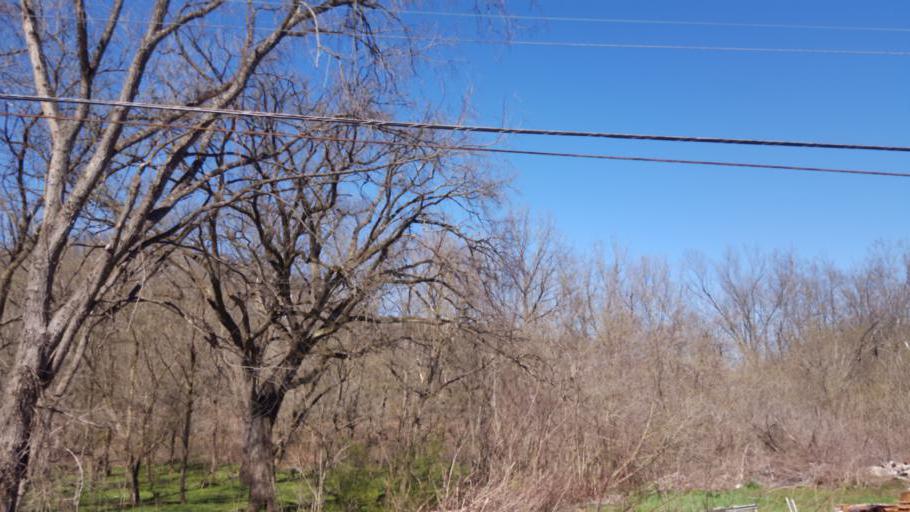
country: US
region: Ohio
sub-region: Jefferson County
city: Tiltonsville
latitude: 40.1837
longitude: -80.6997
